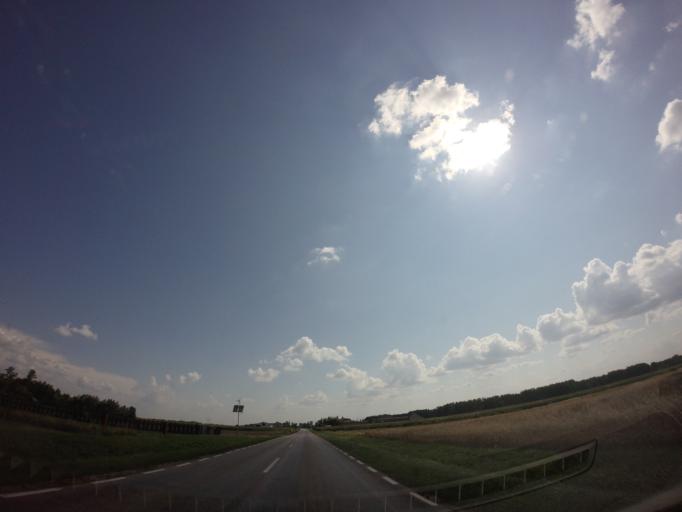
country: PL
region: Podlasie
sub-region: Powiat zambrowski
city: Zambrow
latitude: 52.9077
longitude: 22.2543
